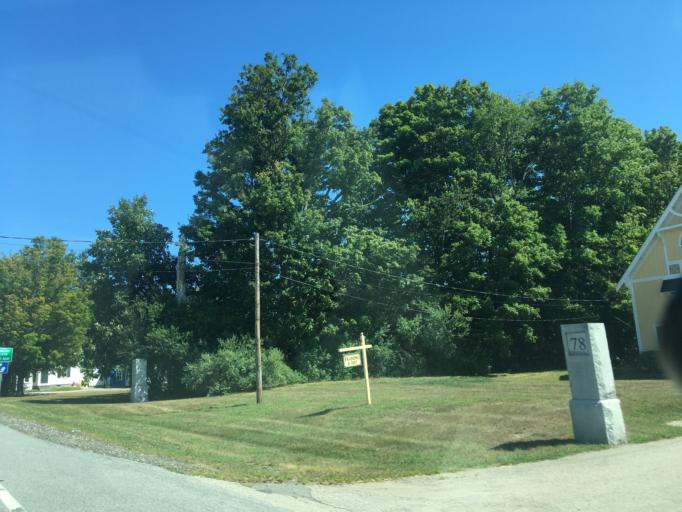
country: US
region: New Hampshire
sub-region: Rockingham County
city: Exeter
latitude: 43.0114
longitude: -70.9178
